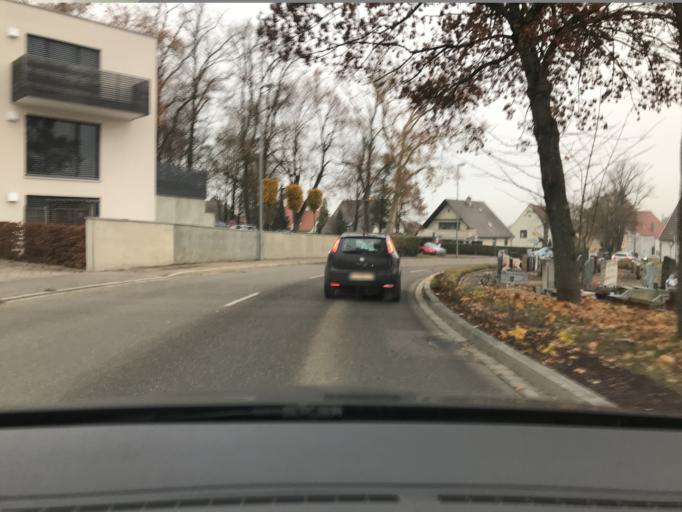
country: DE
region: Bavaria
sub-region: Swabia
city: Noerdlingen
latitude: 48.8470
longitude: 10.4827
